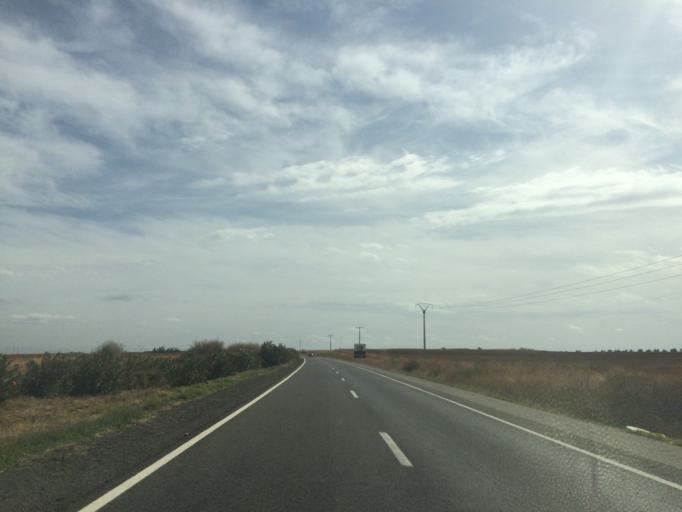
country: MA
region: Meknes-Tafilalet
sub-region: Meknes
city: Meknes
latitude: 33.8362
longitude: -5.5891
